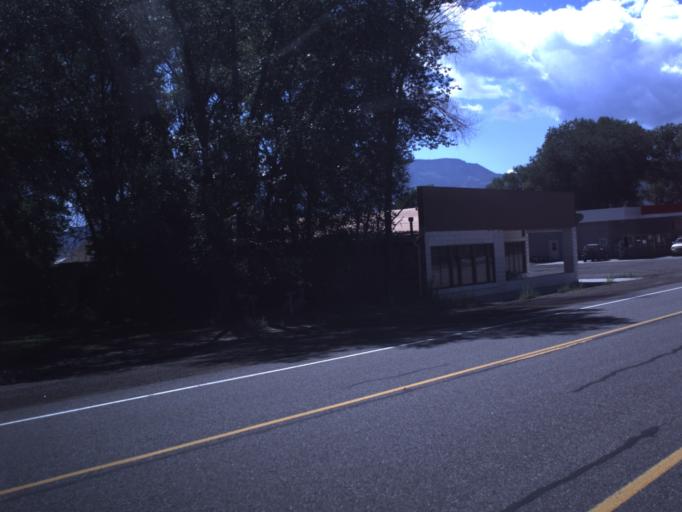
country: US
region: Utah
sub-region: Piute County
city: Junction
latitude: 38.2375
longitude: -112.2200
